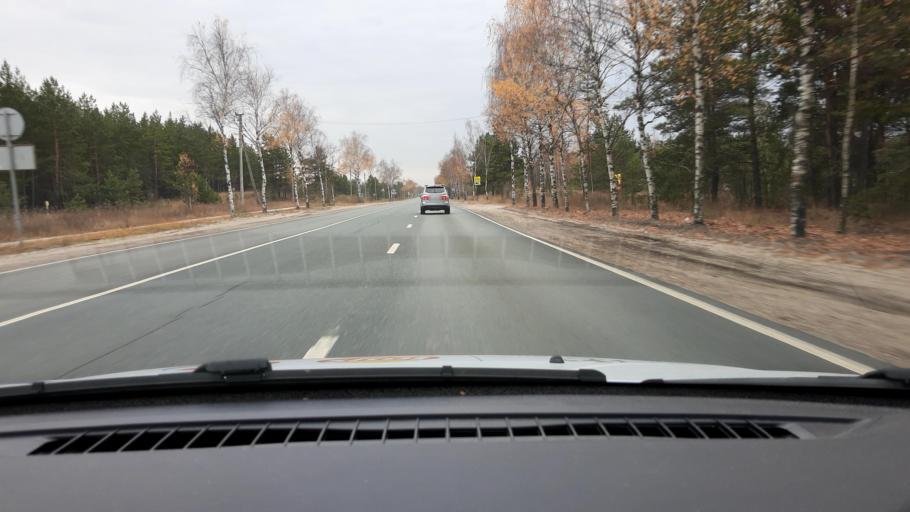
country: RU
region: Nizjnij Novgorod
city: Dzerzhinsk
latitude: 56.2864
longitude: 43.4756
